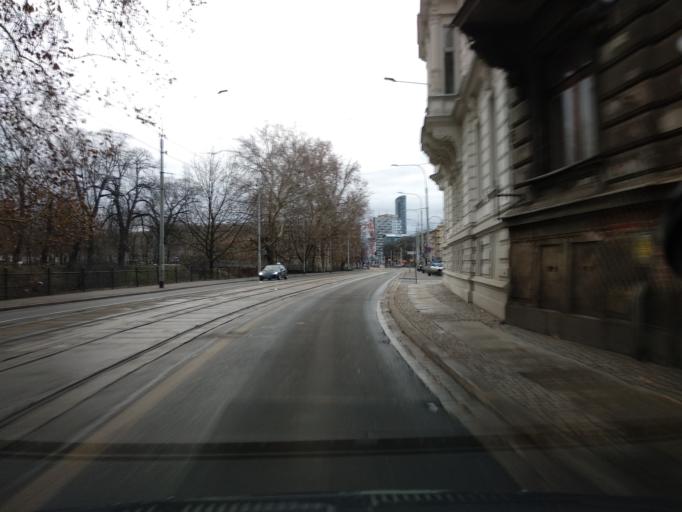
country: PL
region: Lower Silesian Voivodeship
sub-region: Powiat wroclawski
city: Wroclaw
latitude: 51.1096
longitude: 17.0219
